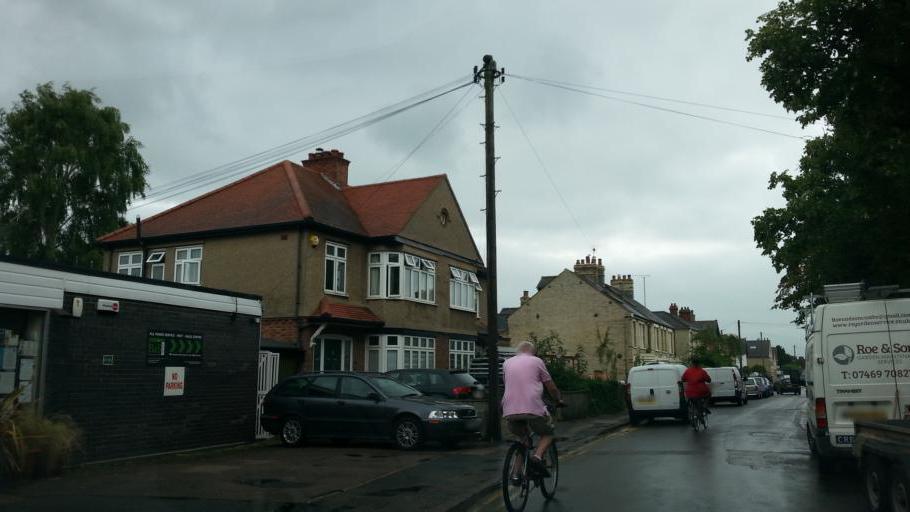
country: GB
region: England
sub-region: Cambridgeshire
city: Histon
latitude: 52.2492
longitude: 0.1073
